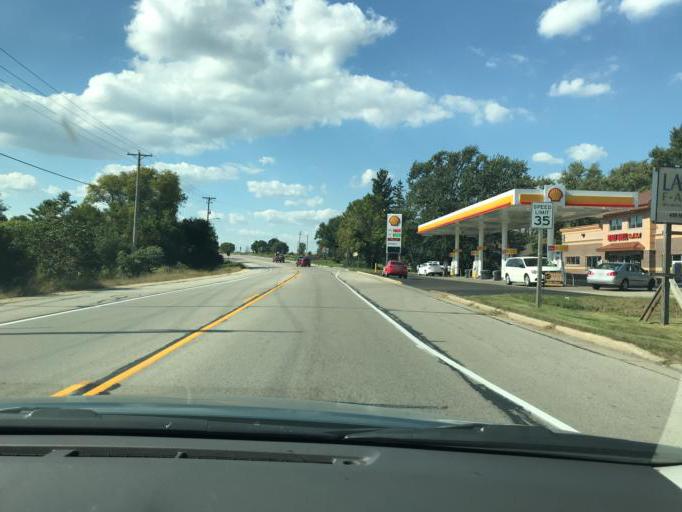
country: US
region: Wisconsin
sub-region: Walworth County
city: Delavan
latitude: 42.6262
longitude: -88.5882
